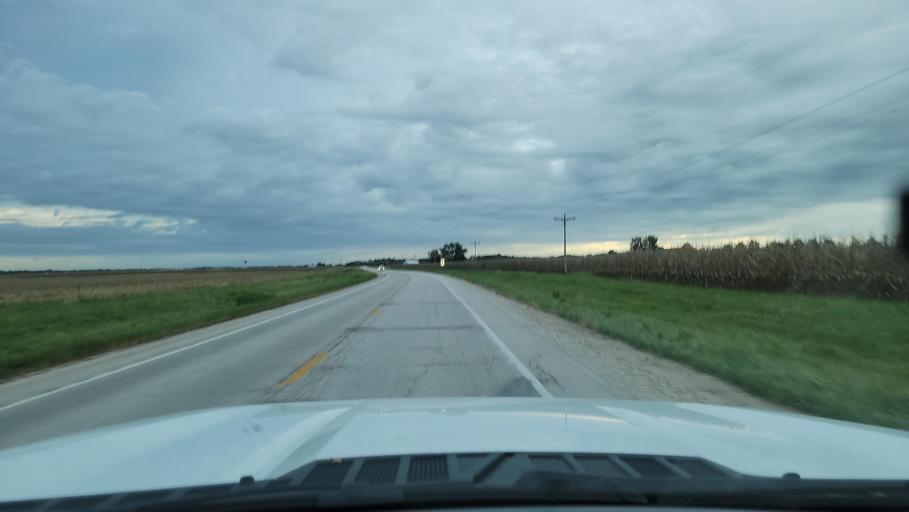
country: US
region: Illinois
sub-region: Schuyler County
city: Rushville
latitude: 40.0970
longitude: -90.6013
